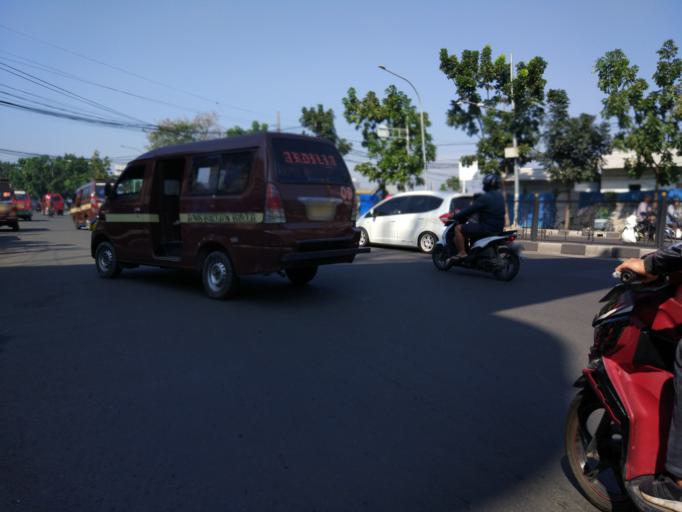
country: ID
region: West Java
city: Bandung
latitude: -6.9138
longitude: 107.6438
